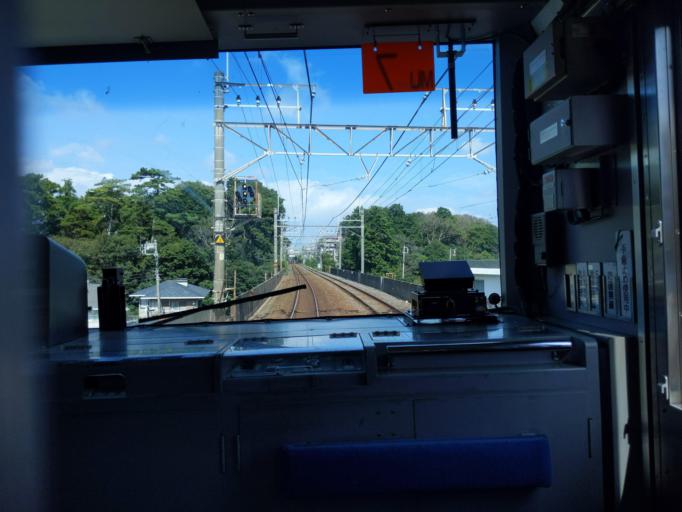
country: JP
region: Chiba
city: Funabashi
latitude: 35.7227
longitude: 139.9682
